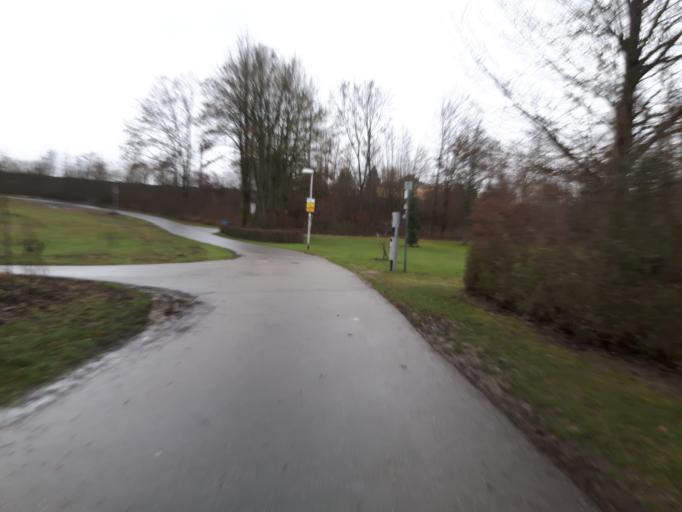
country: DE
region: Baden-Wuerttemberg
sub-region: Regierungsbezirk Stuttgart
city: Bad Rappenau
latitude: 49.2418
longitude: 9.1166
